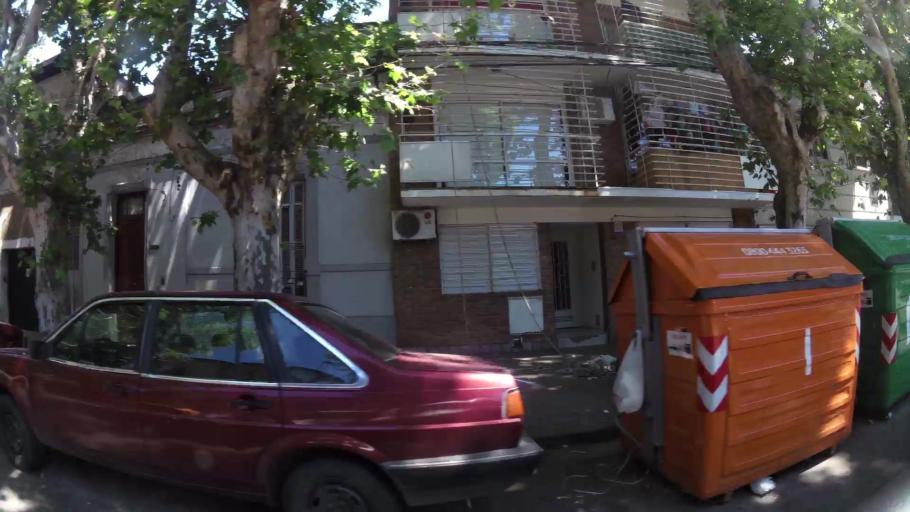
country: AR
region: Santa Fe
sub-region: Departamento de Rosario
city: Rosario
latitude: -32.9365
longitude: -60.6665
